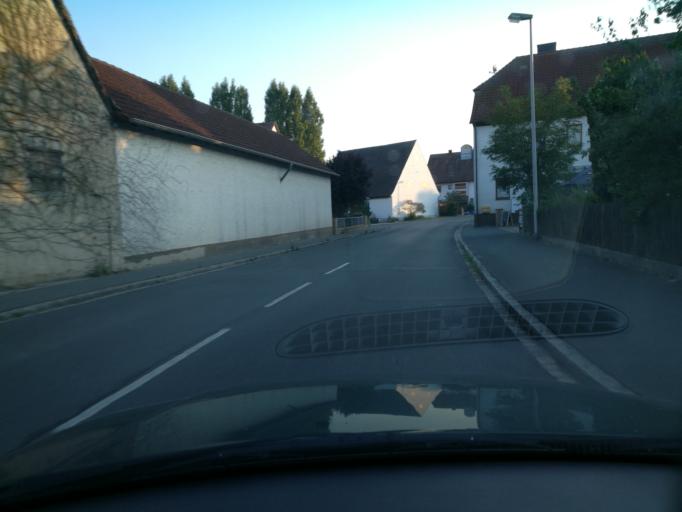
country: DE
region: Bavaria
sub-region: Regierungsbezirk Mittelfranken
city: Hessdorf
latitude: 49.6156
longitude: 10.9086
